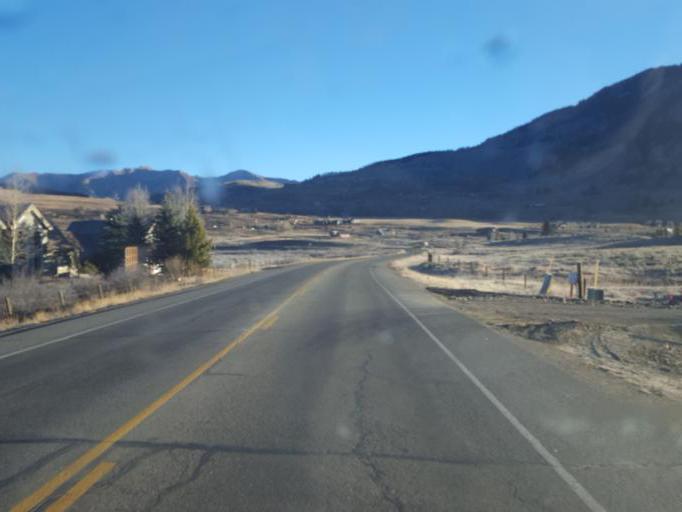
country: US
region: Colorado
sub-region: Gunnison County
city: Crested Butte
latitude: 38.8750
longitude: -106.9798
